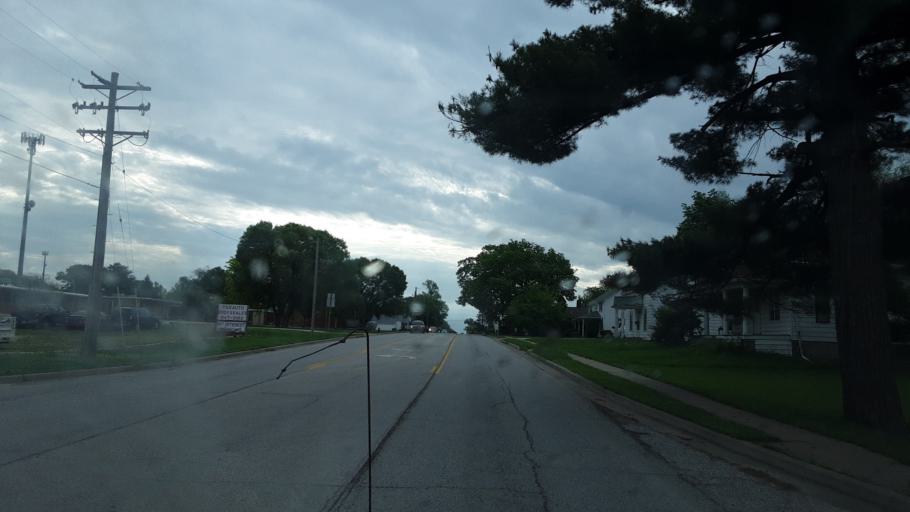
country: US
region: Illinois
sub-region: Hancock County
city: Hamilton
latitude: 40.3964
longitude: -91.3374
